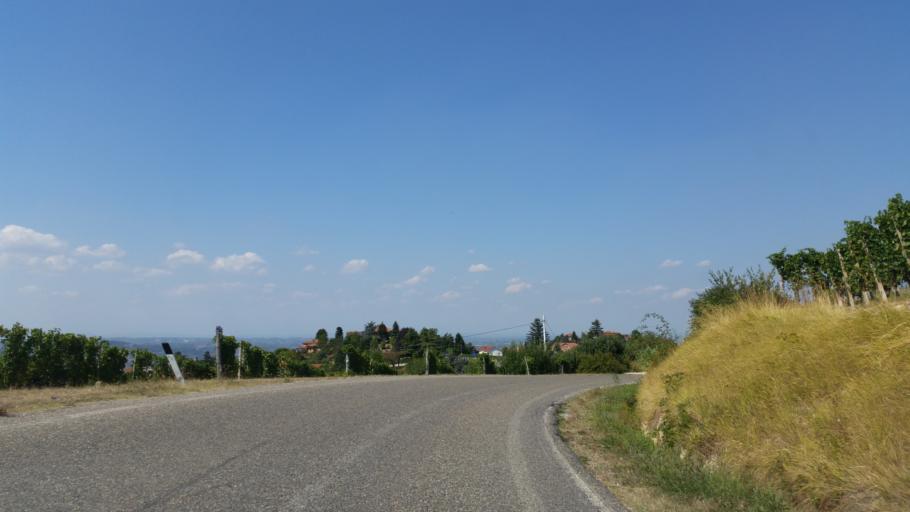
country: IT
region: Piedmont
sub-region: Provincia di Cuneo
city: Treiso
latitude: 44.6854
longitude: 8.0906
